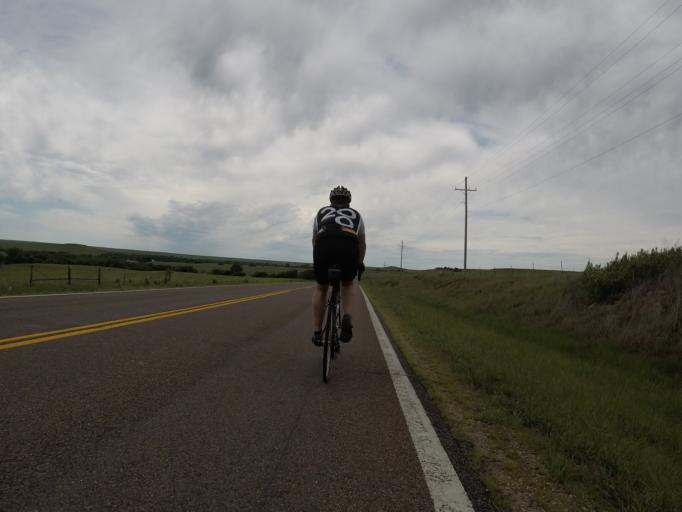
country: US
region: Kansas
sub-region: Wabaunsee County
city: Alma
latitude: 38.8699
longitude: -96.1661
